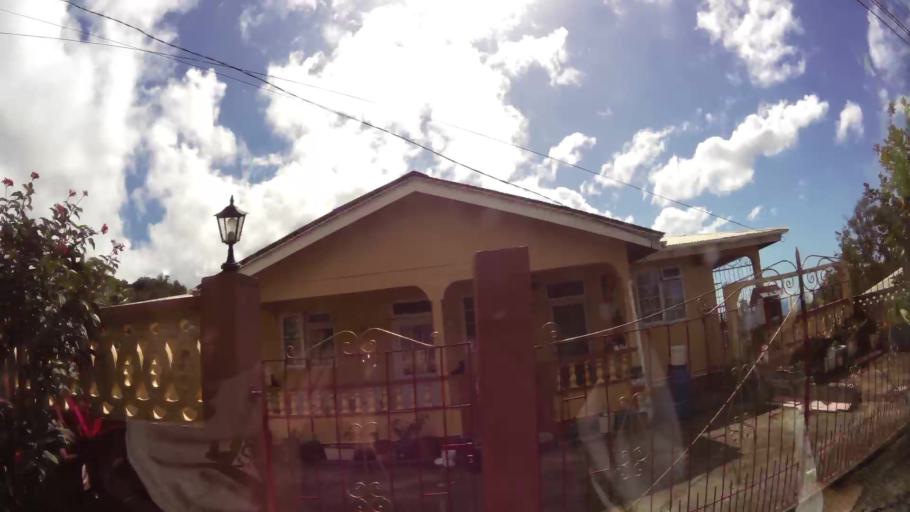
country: DM
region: Saint John
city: Portsmouth
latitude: 15.6059
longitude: -61.4595
